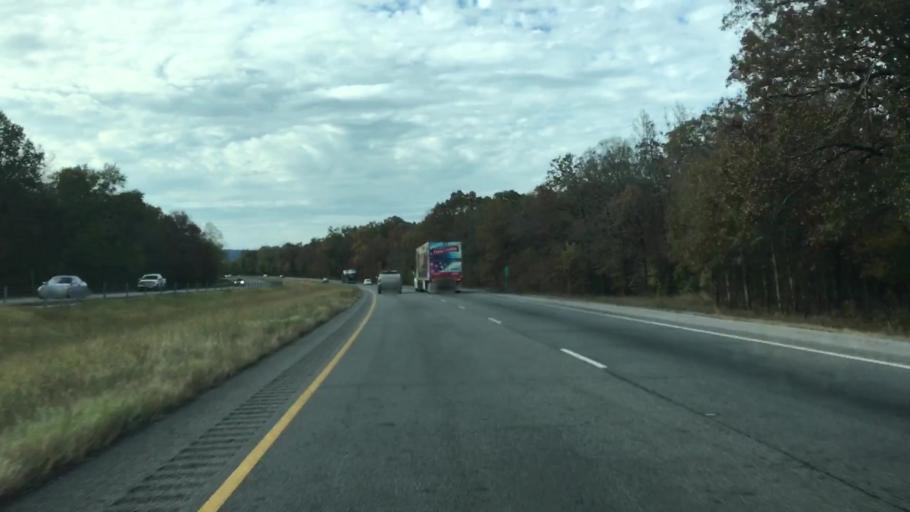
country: US
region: Arkansas
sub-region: Pope County
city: Atkins
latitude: 35.2449
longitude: -92.8643
